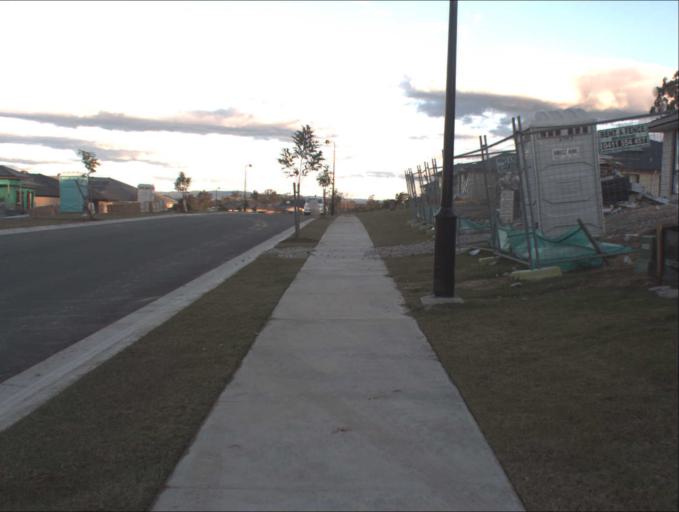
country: AU
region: Queensland
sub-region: Logan
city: North Maclean
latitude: -27.7990
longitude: 152.9529
